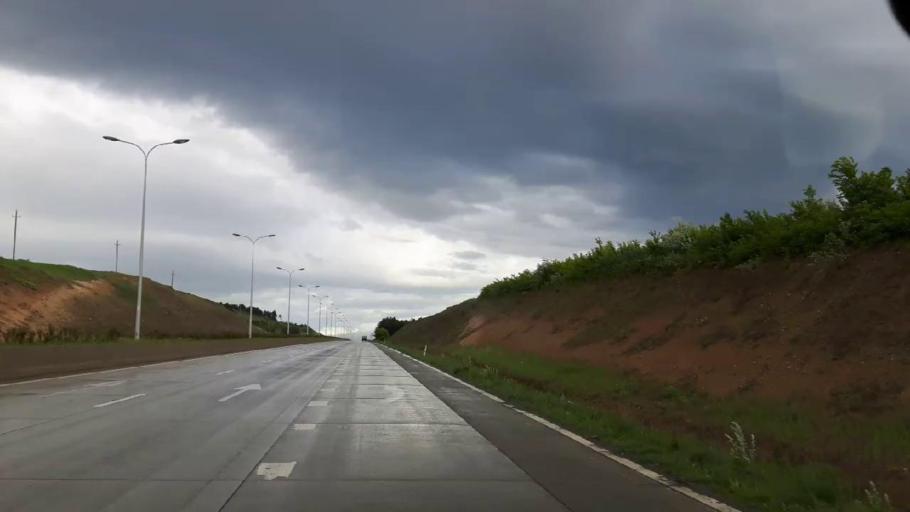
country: GE
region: Shida Kartli
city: Gori
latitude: 42.0120
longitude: 44.0372
